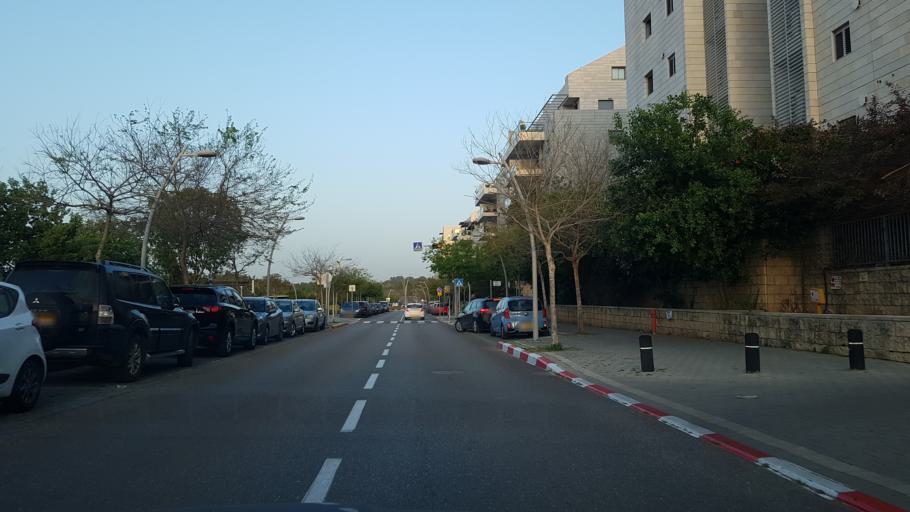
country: IL
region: Central District
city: Ra'anana
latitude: 32.1977
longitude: 34.8918
